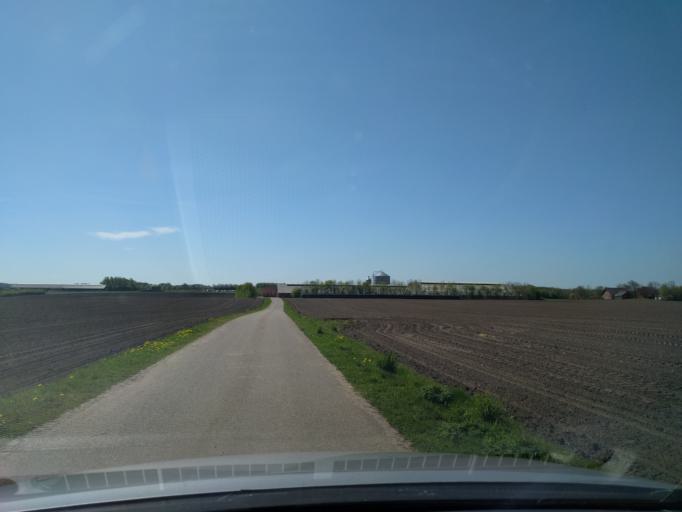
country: DK
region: South Denmark
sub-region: Varde Kommune
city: Olgod
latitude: 55.7945
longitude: 8.6595
